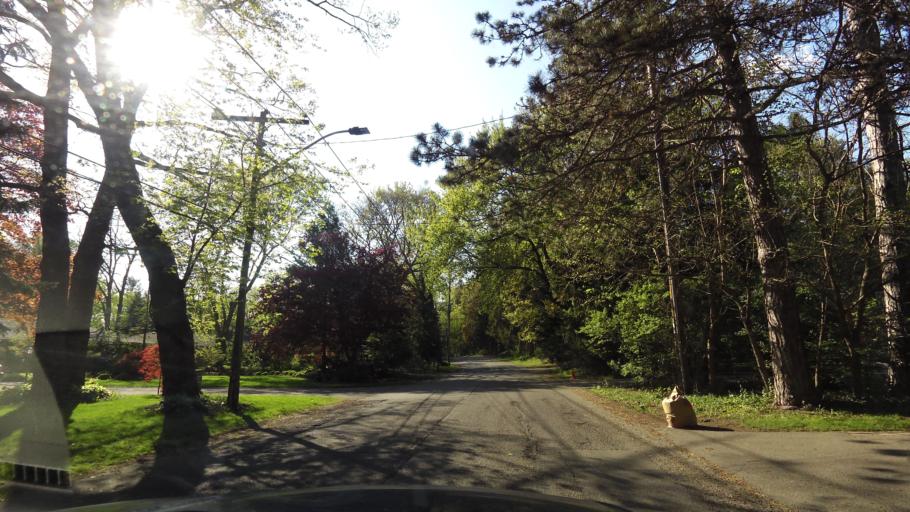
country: CA
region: Ontario
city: Mississauga
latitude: 43.5570
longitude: -79.6043
